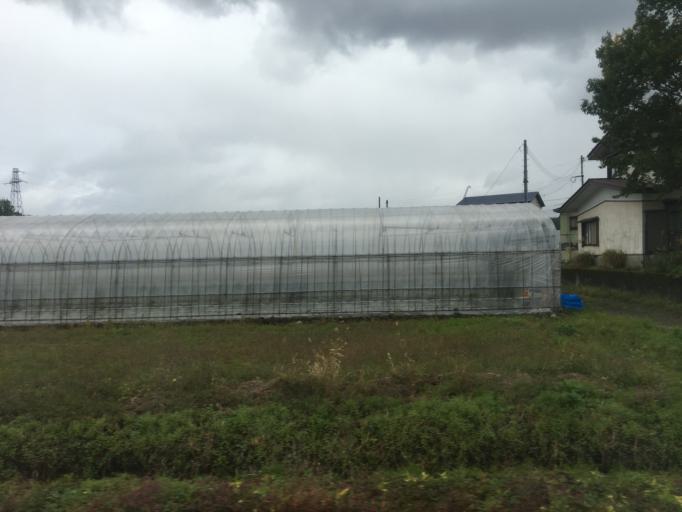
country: JP
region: Yamagata
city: Nagai
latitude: 38.0675
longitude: 139.7433
